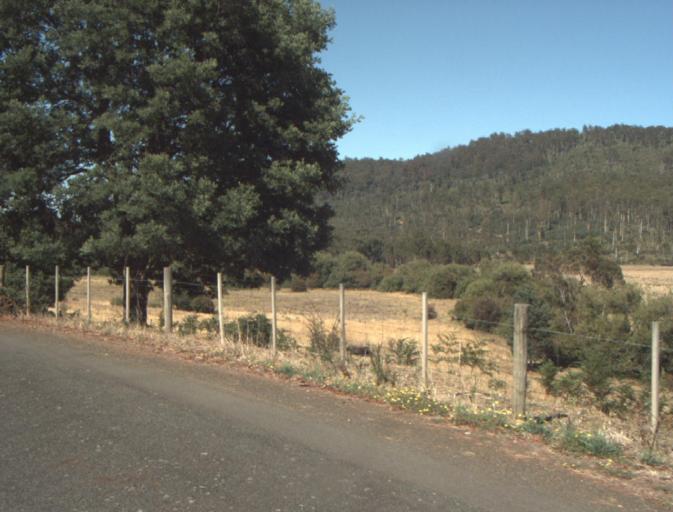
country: AU
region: Tasmania
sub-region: Launceston
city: Newstead
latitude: -41.3504
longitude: 147.3034
